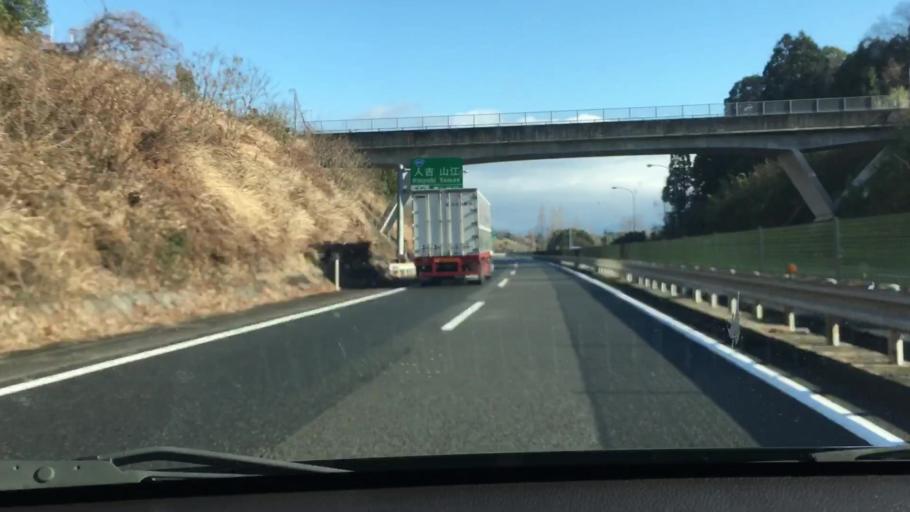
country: JP
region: Kumamoto
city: Hitoyoshi
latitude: 32.2339
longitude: 130.7670
